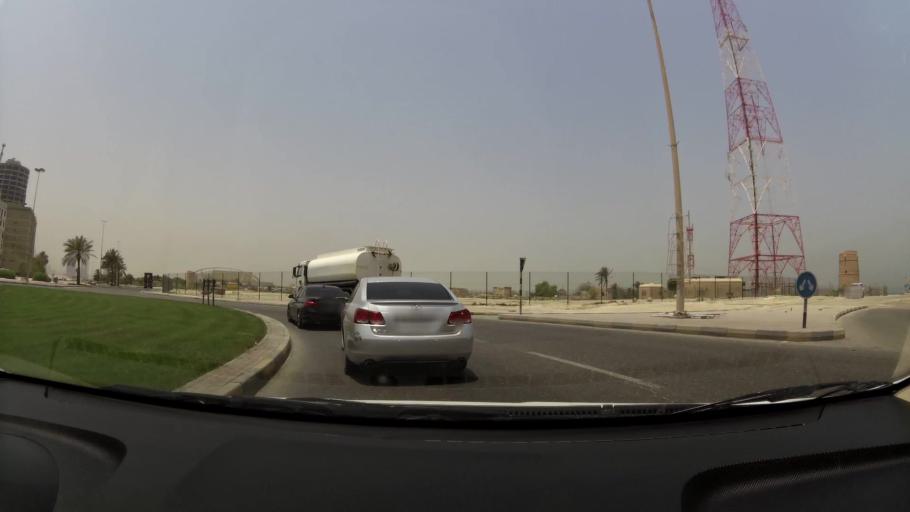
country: AE
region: Ash Shariqah
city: Sharjah
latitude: 25.3350
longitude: 55.3607
